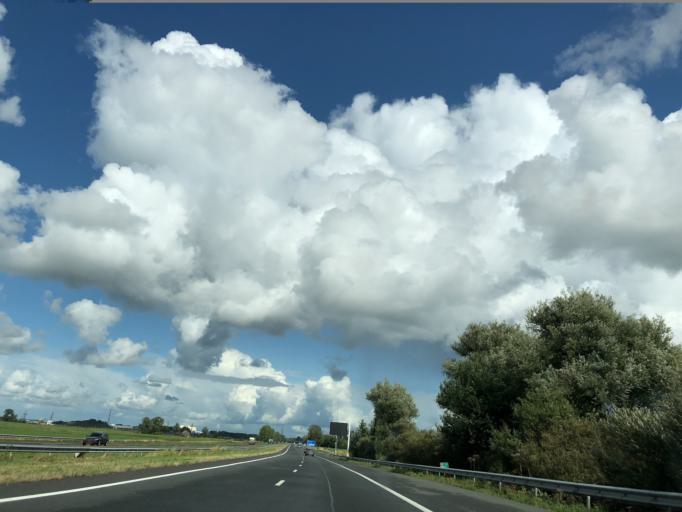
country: NL
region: Groningen
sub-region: Gemeente Zuidhorn
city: Aduard
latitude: 53.1971
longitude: 6.4504
